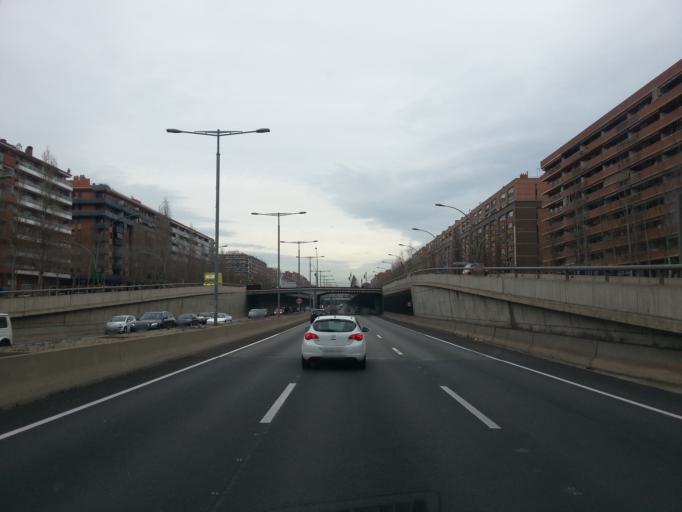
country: ES
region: Catalonia
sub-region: Provincia de Barcelona
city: Sant Marti
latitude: 41.4085
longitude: 2.1938
